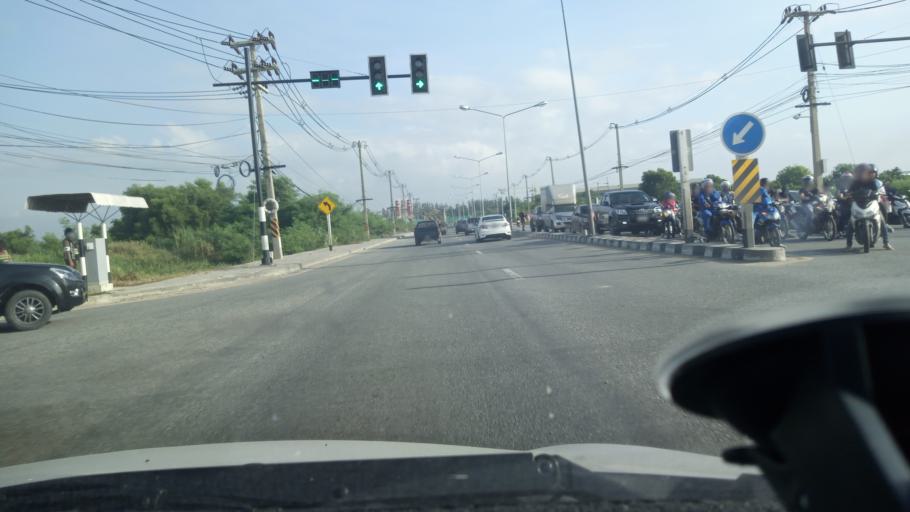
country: TH
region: Chon Buri
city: Phan Thong
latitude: 13.4438
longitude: 101.1035
